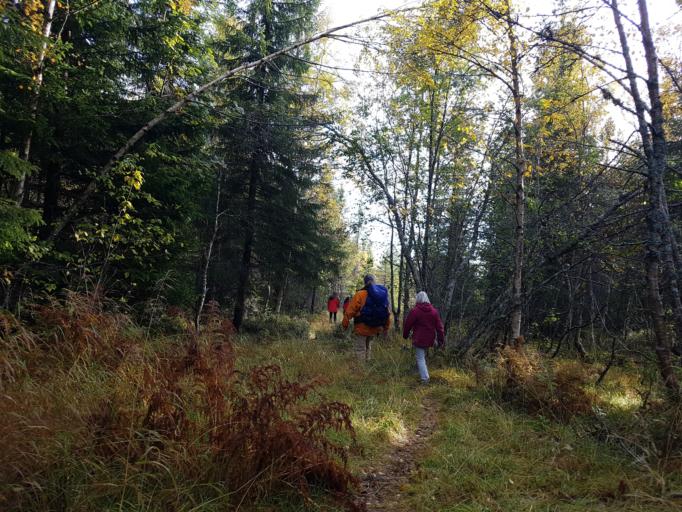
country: NO
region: Sor-Trondelag
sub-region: Trondheim
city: Trondheim
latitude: 63.4242
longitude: 10.2845
